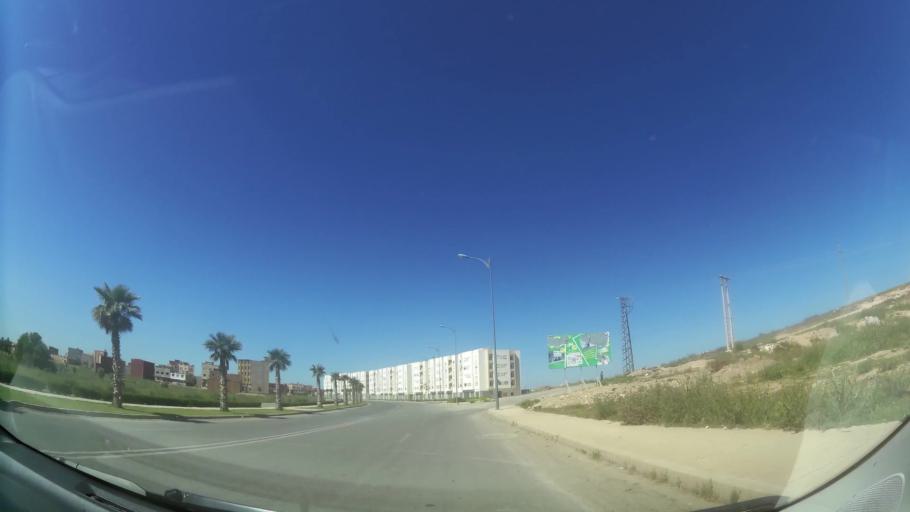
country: MA
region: Oriental
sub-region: Oujda-Angad
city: Oujda
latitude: 34.6694
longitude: -1.8604
